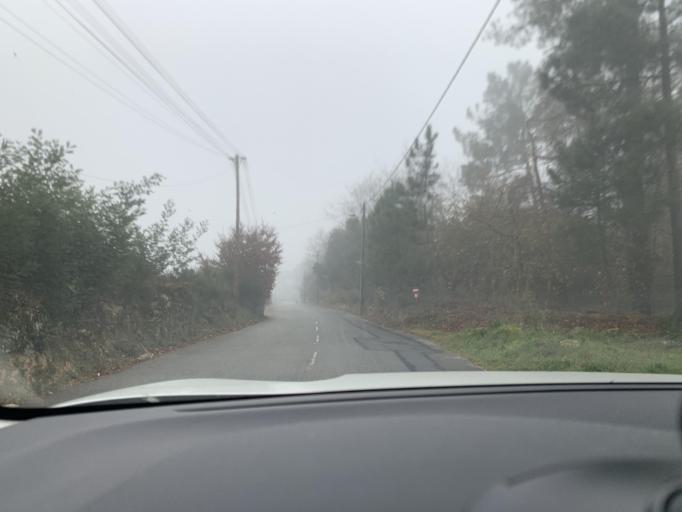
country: PT
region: Viseu
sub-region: Viseu
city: Viseu
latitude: 40.6308
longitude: -7.9204
